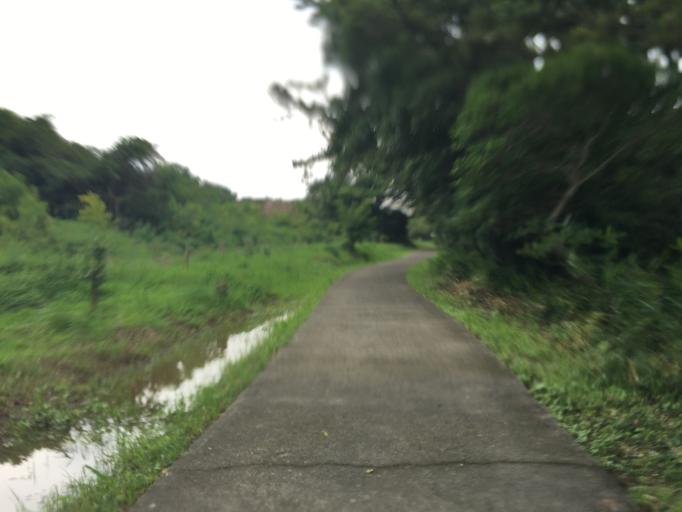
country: JP
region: Aichi
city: Ishiki
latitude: 34.7176
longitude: 137.0496
